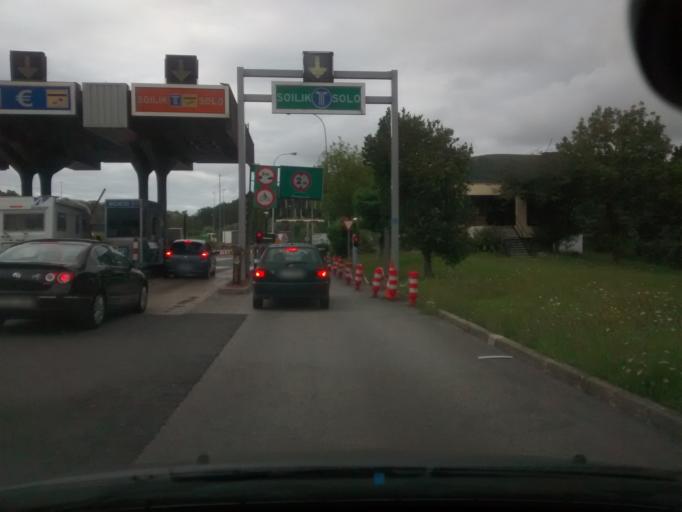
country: ES
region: Basque Country
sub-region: Provincia de Guipuzcoa
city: Cestona
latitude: 43.2673
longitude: -2.2727
